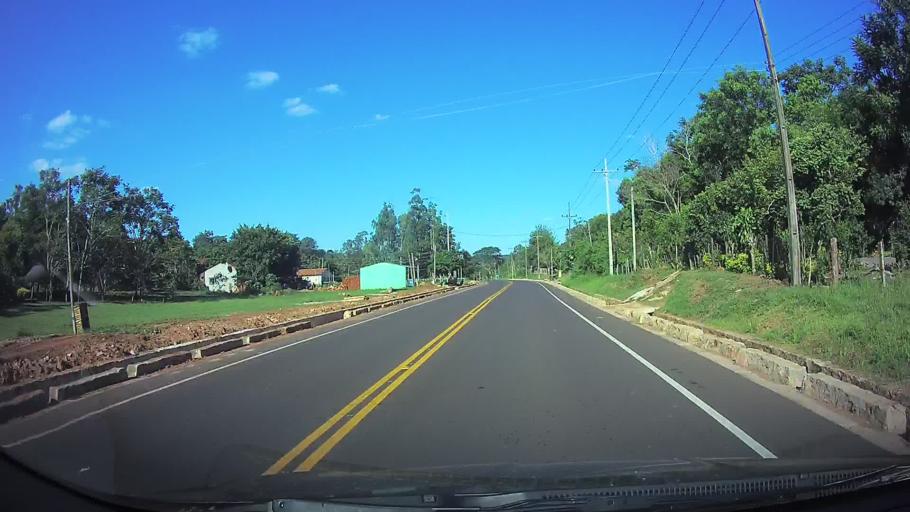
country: PY
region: Cordillera
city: Caacupe
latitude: -25.3249
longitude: -57.1563
